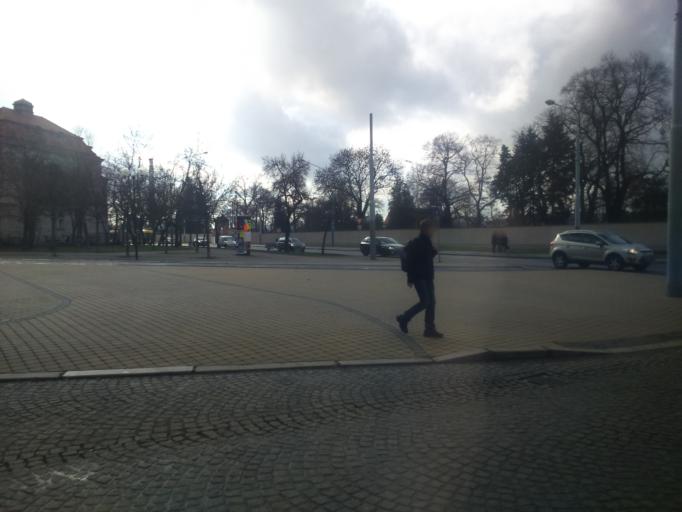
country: CZ
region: Plzensky
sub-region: Okres Plzen-Mesto
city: Pilsen
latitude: 49.7405
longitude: 13.3869
